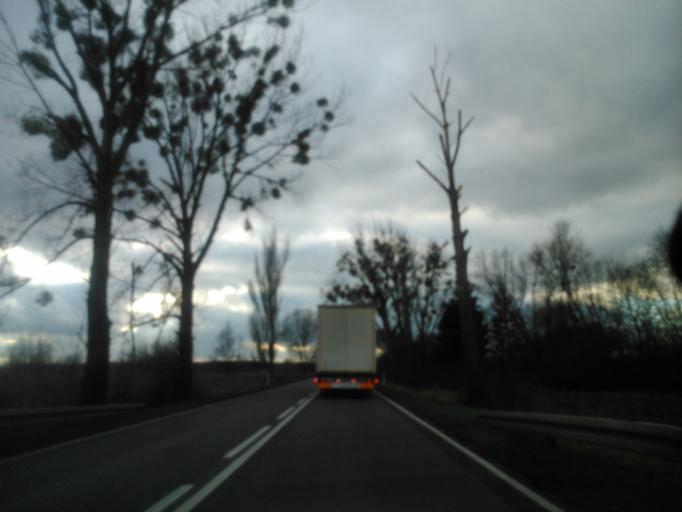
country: PL
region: Masovian Voivodeship
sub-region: Powiat nowodworski
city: Nowy Dwor Mazowiecki
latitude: 52.4056
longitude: 20.6887
